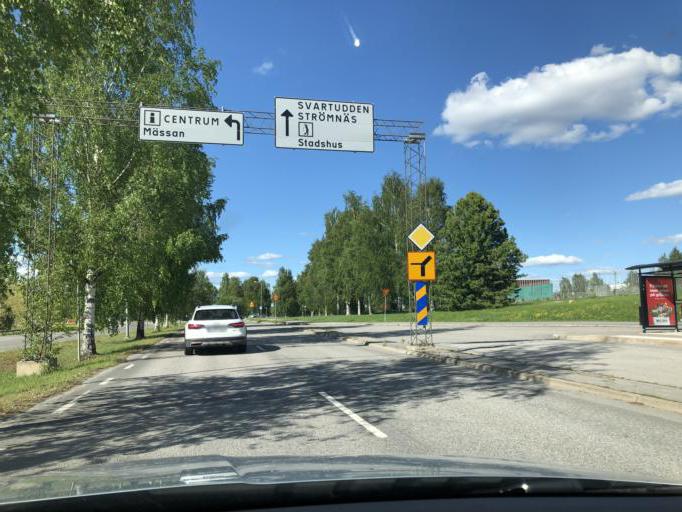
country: SE
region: Norrbotten
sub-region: Pitea Kommun
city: Pitea
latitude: 65.3140
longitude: 21.4921
